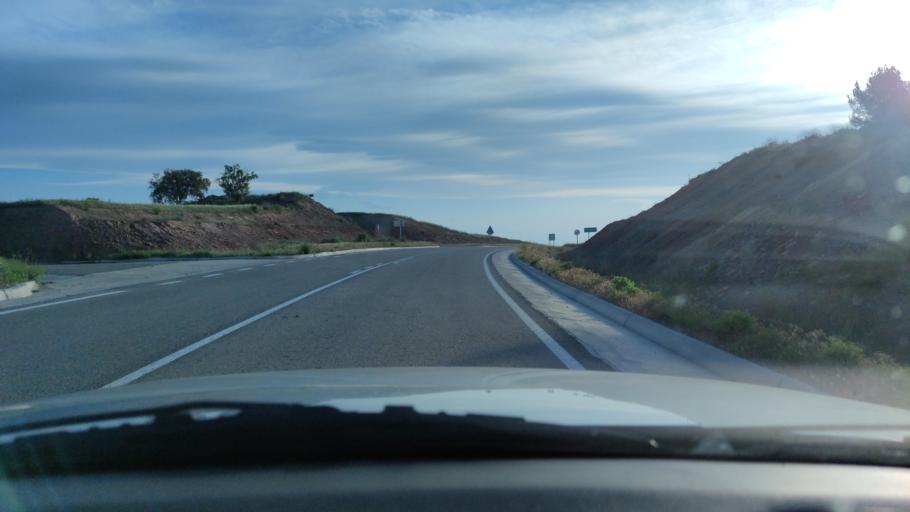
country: ES
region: Catalonia
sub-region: Provincia de Lleida
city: Castellsera
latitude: 41.7721
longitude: 1.0246
